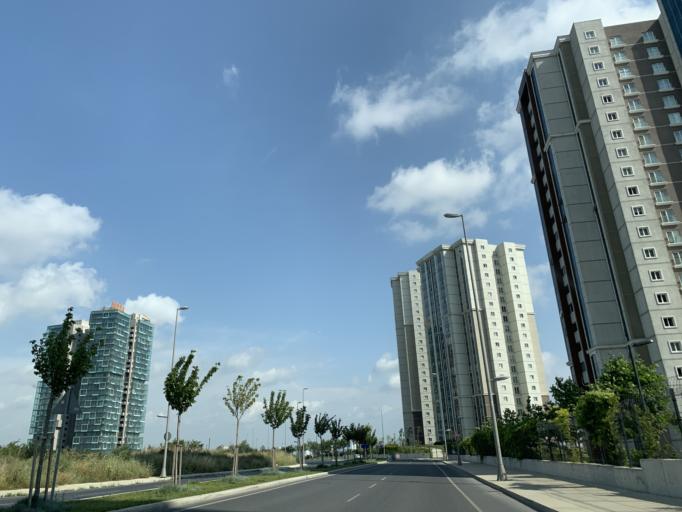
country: TR
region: Istanbul
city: Esenyurt
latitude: 41.0779
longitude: 28.6965
